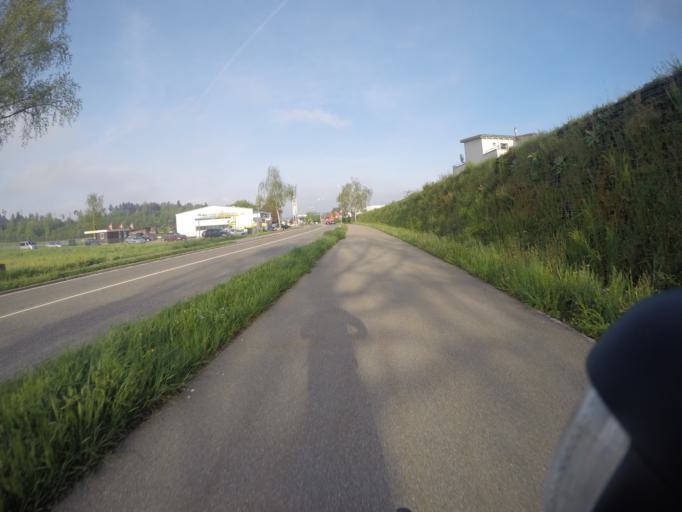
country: CH
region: Zurich
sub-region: Bezirk Uster
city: Bruttisellen
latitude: 47.4288
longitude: 8.6456
